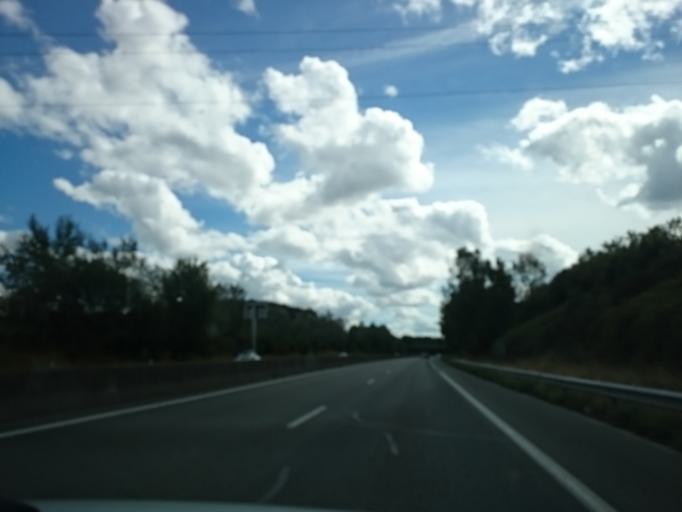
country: FR
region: Pays de la Loire
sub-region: Departement de la Loire-Atlantique
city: Basse-Goulaine
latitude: 47.2032
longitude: -1.4840
